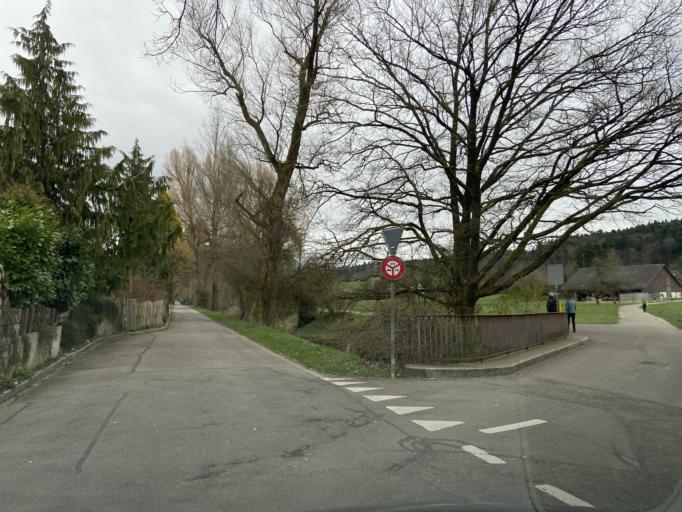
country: CH
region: Zurich
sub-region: Bezirk Winterthur
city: Mattenbach (Kreis 7)
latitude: 47.4882
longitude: 8.7471
